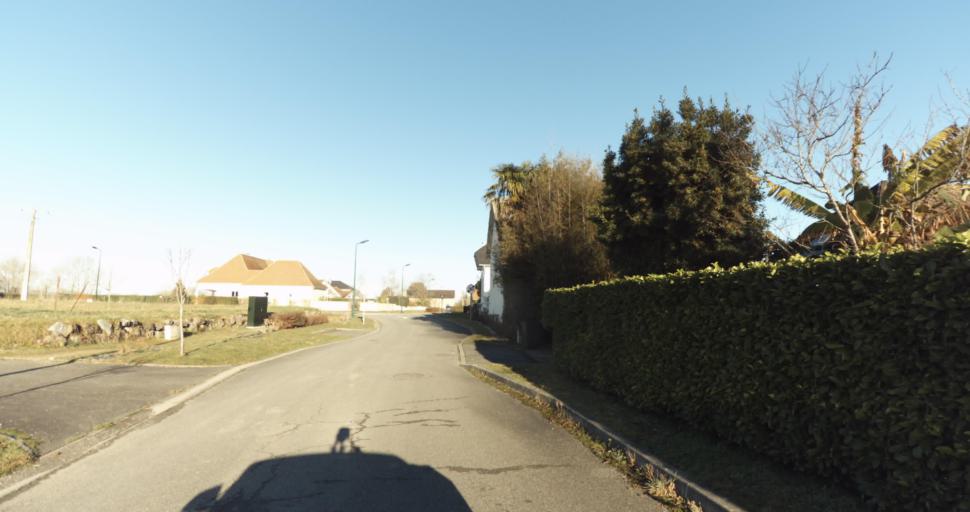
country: FR
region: Aquitaine
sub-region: Departement des Pyrenees-Atlantiques
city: Morlaas
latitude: 43.3285
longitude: -0.2599
